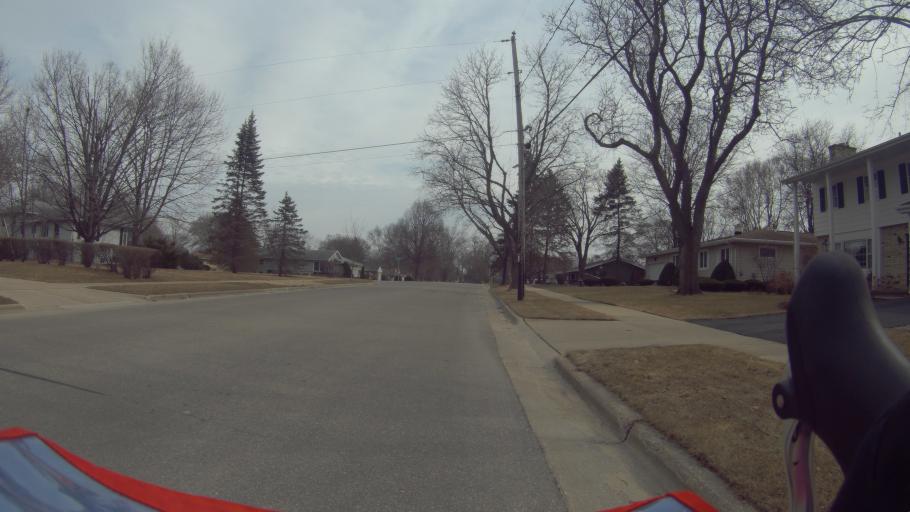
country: US
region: Wisconsin
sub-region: Dane County
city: Maple Bluff
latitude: 43.1214
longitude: -89.3700
